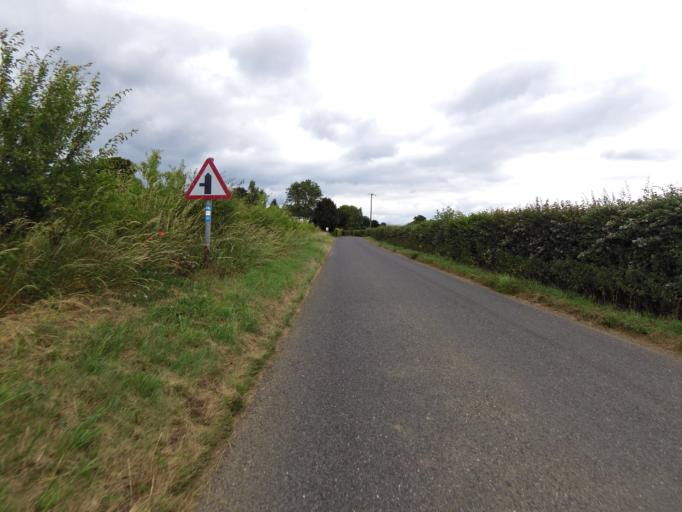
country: GB
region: England
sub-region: Norfolk
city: Harleston
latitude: 52.4276
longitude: 1.3591
